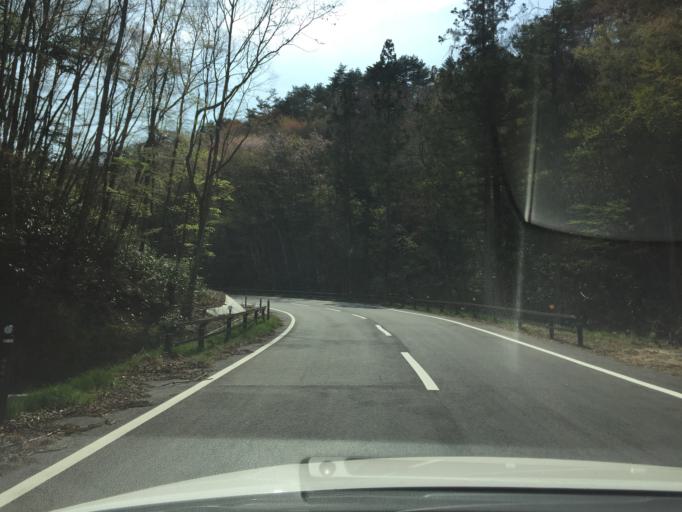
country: JP
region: Fukushima
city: Iwaki
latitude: 37.2500
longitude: 140.8498
